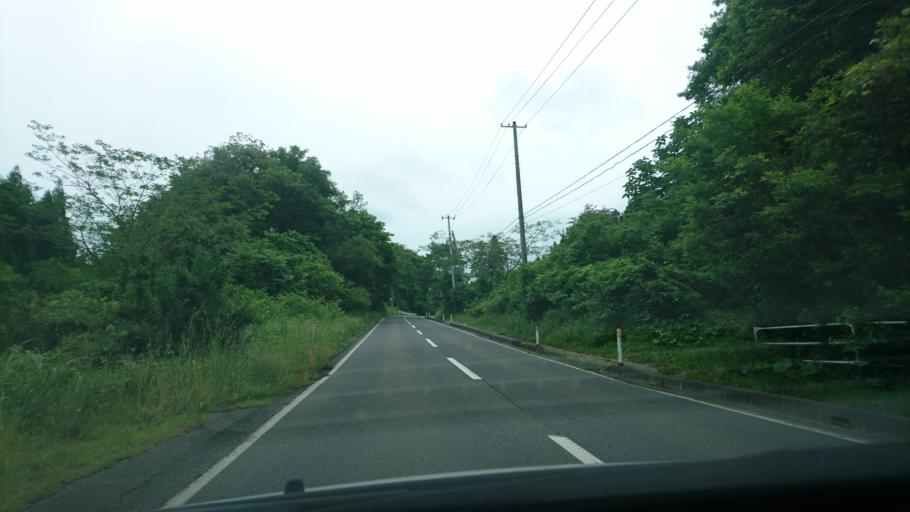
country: JP
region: Iwate
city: Ichinoseki
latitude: 38.9592
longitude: 141.0558
